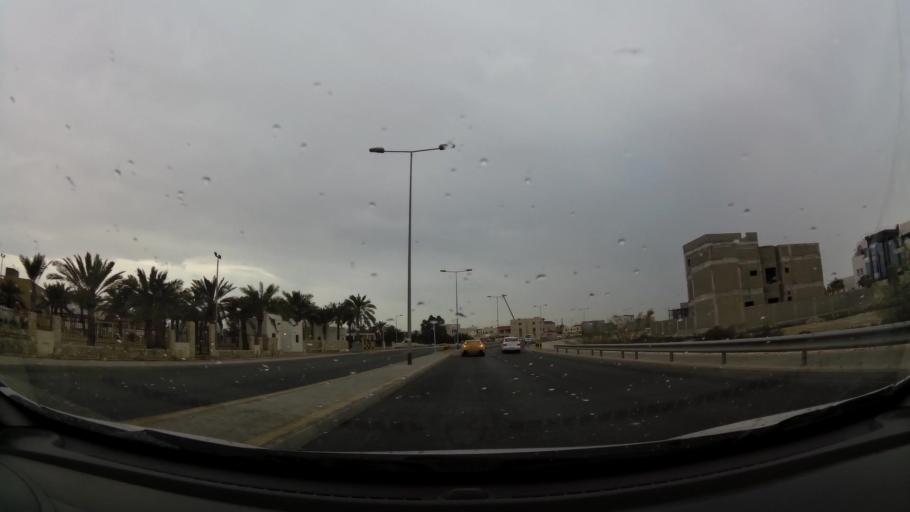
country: BH
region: Central Governorate
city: Madinat Hamad
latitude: 26.1312
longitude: 50.4925
